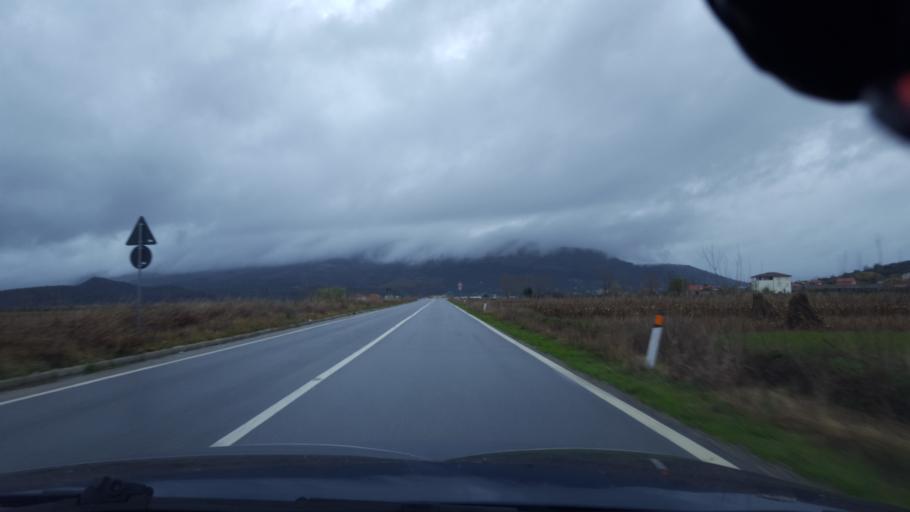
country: AL
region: Shkoder
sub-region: Rrethi i Shkodres
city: Berdica e Madhe
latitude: 42.0031
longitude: 19.4808
